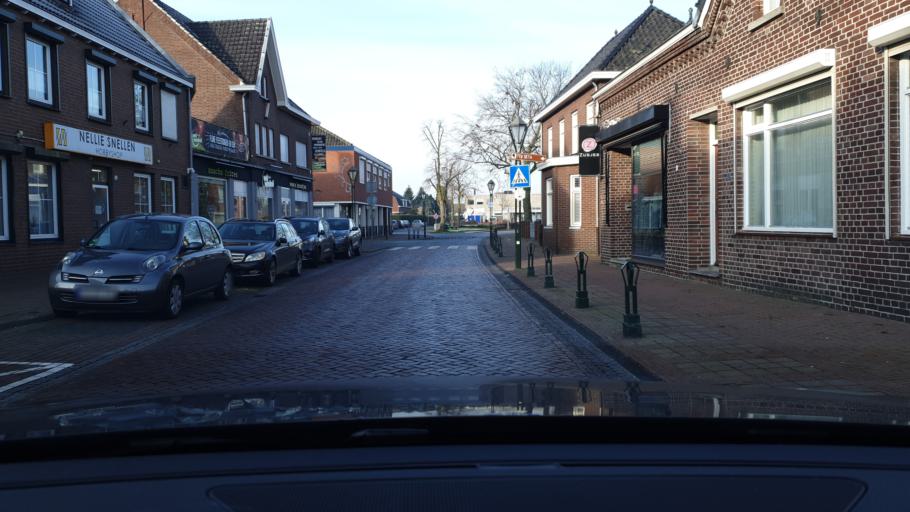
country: NL
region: Limburg
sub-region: Gemeente Peel en Maas
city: Maasbree
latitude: 51.4125
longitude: 6.0358
